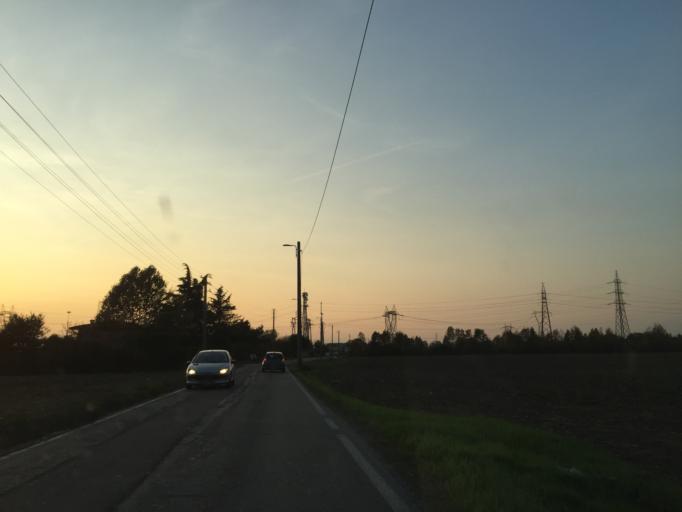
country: IT
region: Lombardy
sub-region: Provincia di Brescia
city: Folzano
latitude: 45.4914
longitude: 10.1995
